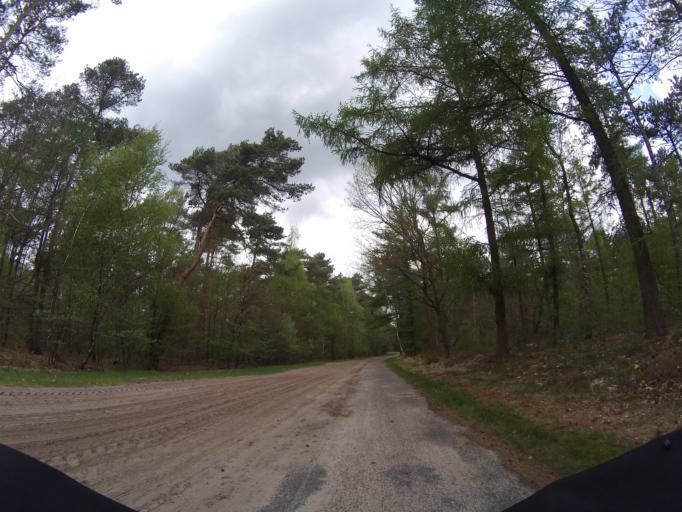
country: NL
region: Overijssel
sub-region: Gemeente Twenterand
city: Magele
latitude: 52.5299
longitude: 6.5458
